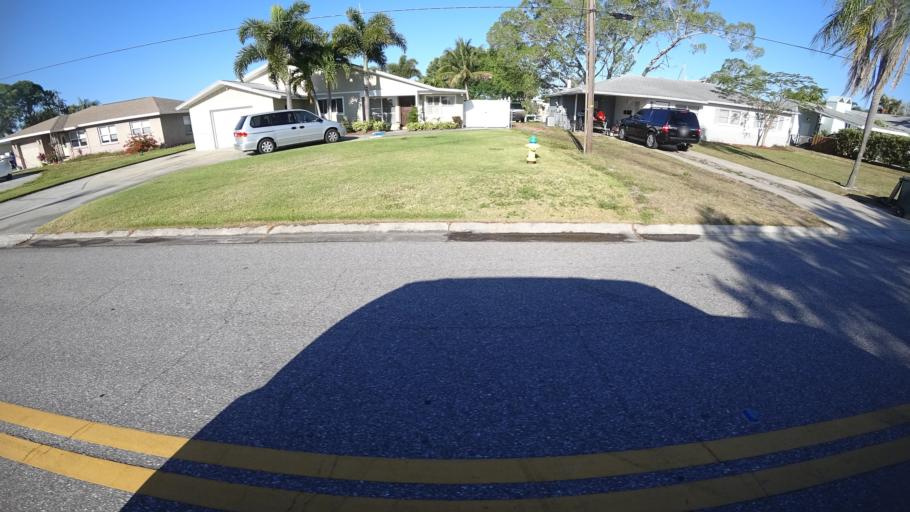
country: US
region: Florida
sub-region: Manatee County
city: Bayshore Gardens
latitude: 27.4202
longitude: -82.5878
